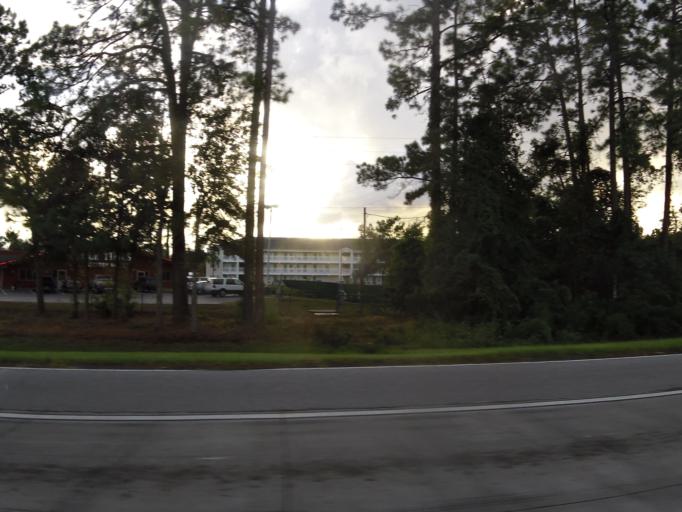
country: US
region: Georgia
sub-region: Glynn County
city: Dock Junction
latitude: 31.2201
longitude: -81.4937
